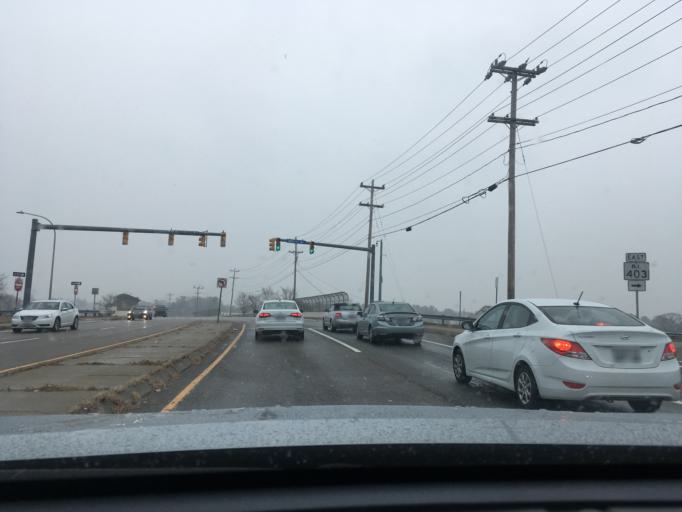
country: US
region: Rhode Island
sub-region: Washington County
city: North Kingstown
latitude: 41.6029
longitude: -71.4545
